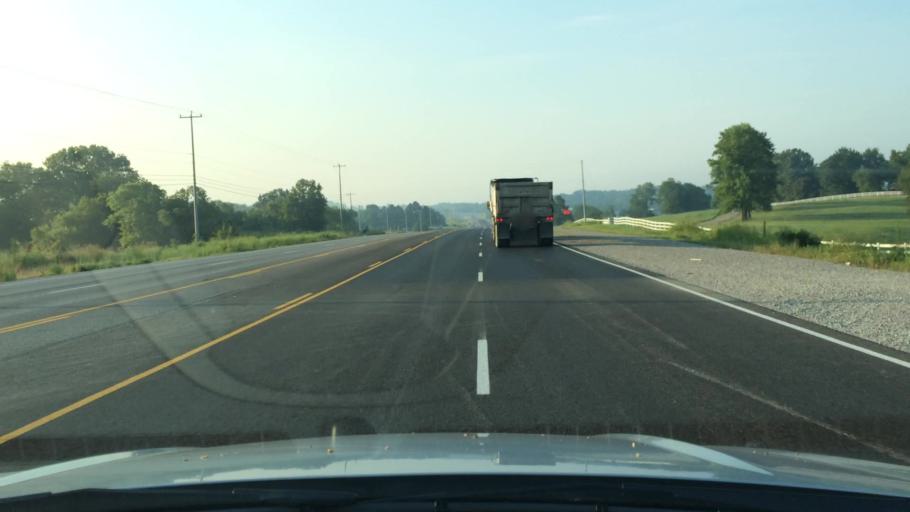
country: US
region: Tennessee
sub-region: Giles County
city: Pulaski
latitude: 35.1616
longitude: -87.0100
